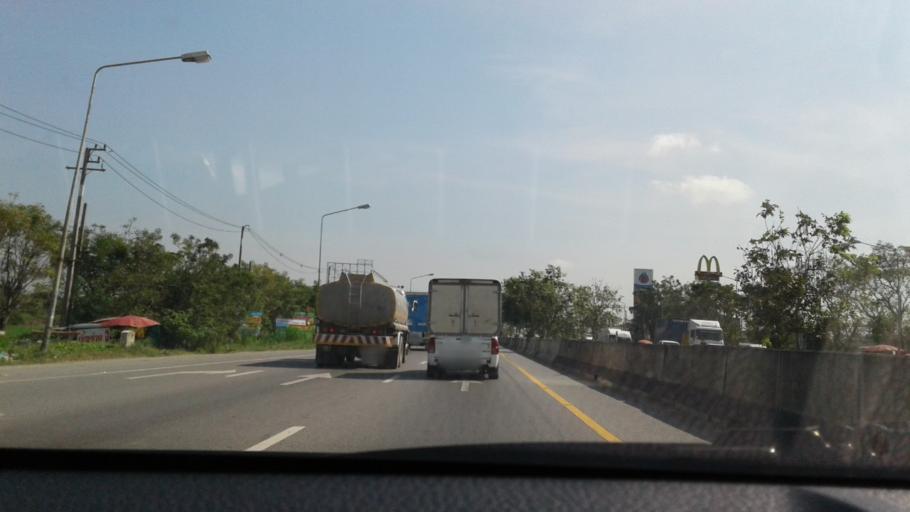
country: TH
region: Nonthaburi
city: Pak Kret
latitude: 13.9553
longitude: 100.4855
